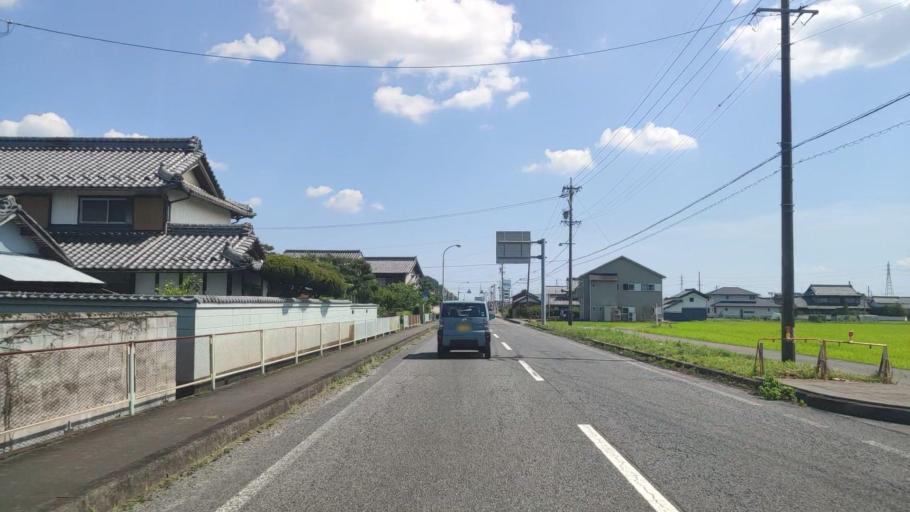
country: JP
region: Gifu
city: Godo
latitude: 35.4843
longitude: 136.6739
